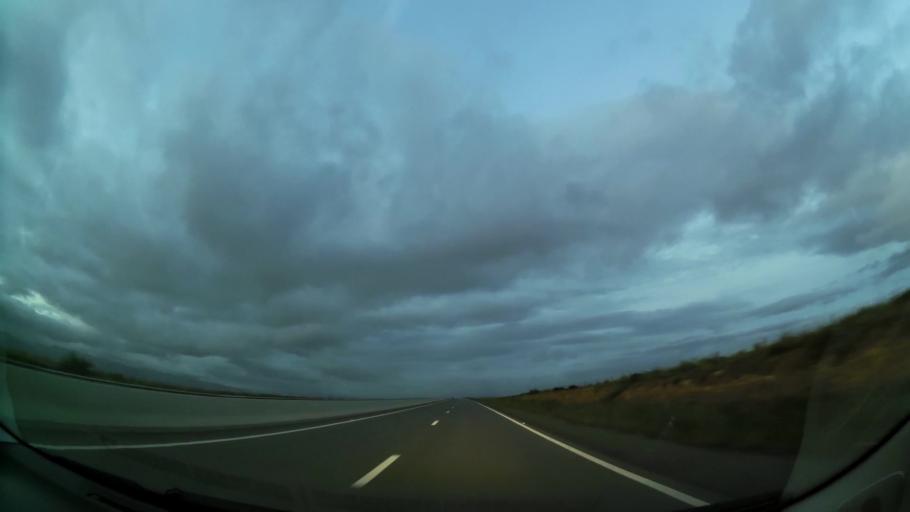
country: MA
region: Oriental
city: El Aioun
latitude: 34.6295
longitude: -2.3538
